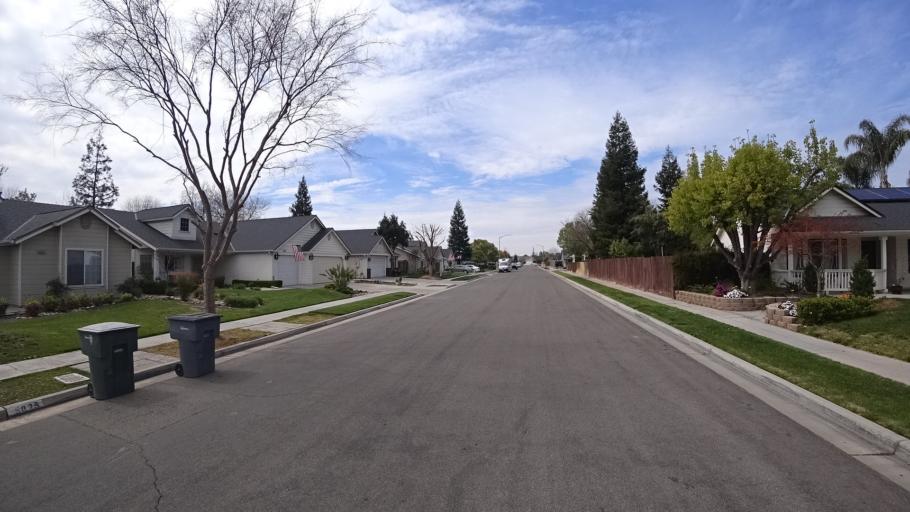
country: US
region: California
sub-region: Fresno County
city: Biola
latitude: 36.8317
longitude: -119.8954
